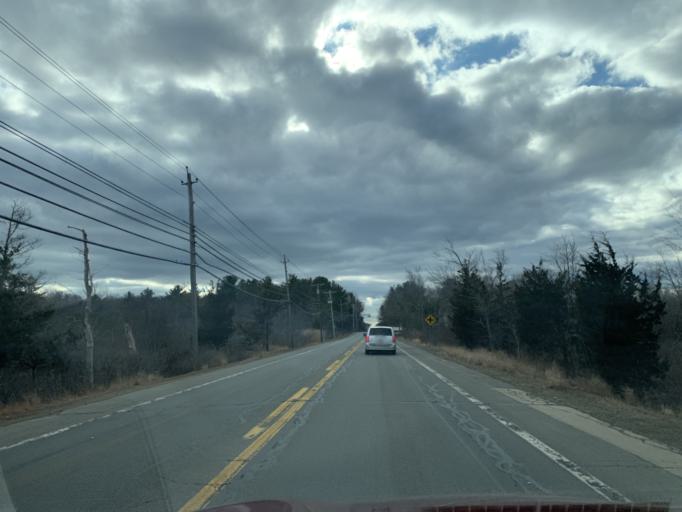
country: US
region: Massachusetts
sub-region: Essex County
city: Newburyport
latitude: 42.7770
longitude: -70.8841
